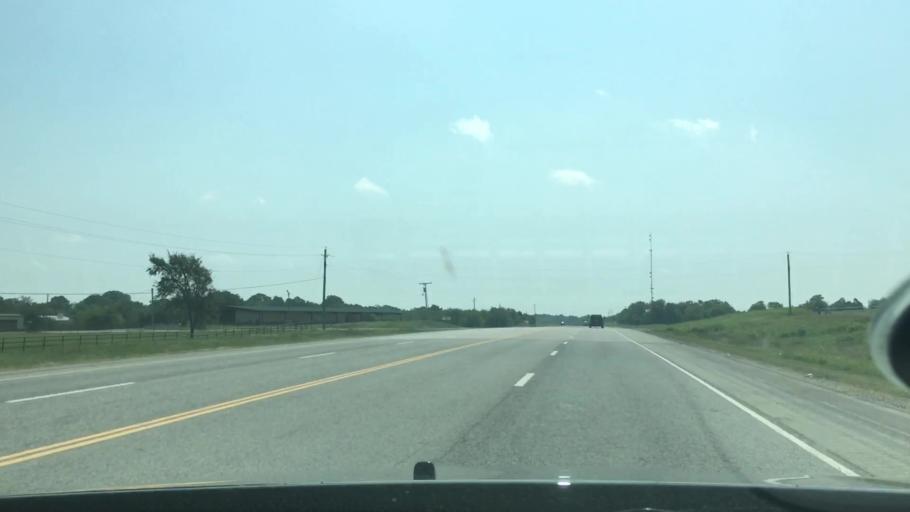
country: US
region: Oklahoma
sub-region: Atoka County
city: Atoka
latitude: 34.3637
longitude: -96.0991
